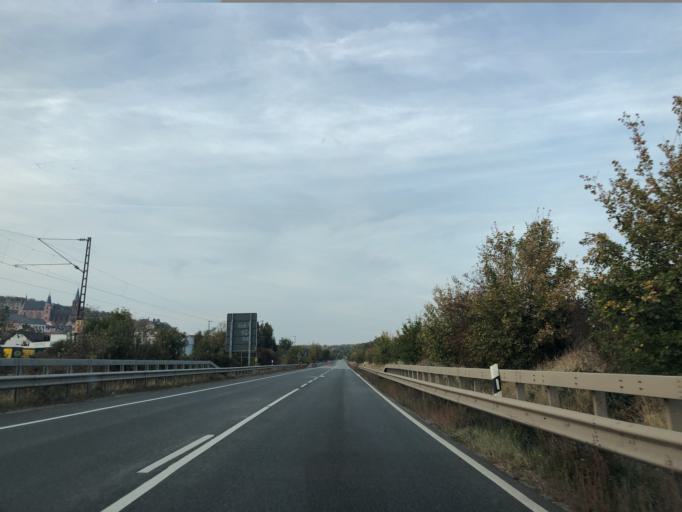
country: DE
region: Rheinland-Pfalz
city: Oppenheim
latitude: 49.8463
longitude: 8.3585
